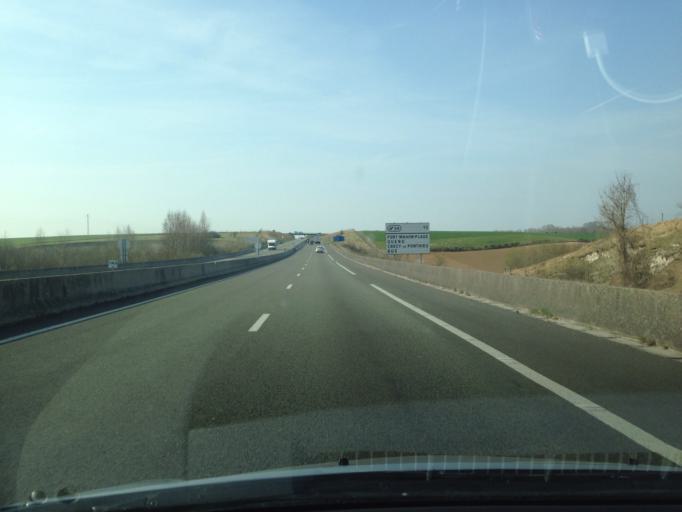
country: FR
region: Picardie
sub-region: Departement de la Somme
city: Sailly-Flibeaucourt
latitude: 50.1443
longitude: 1.8035
